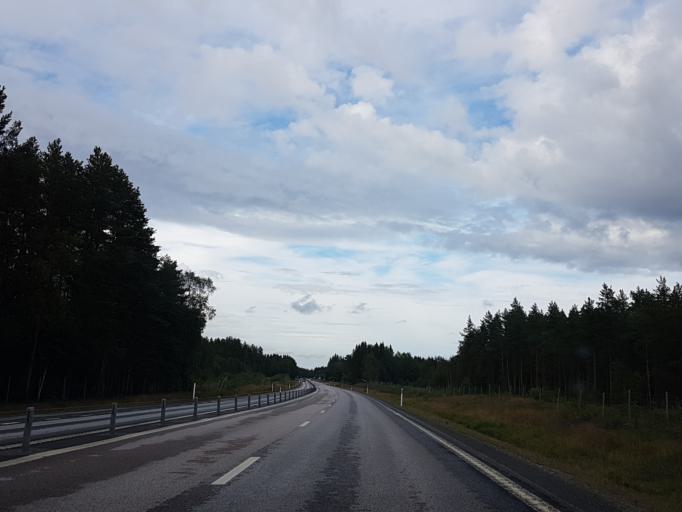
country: SE
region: Vaesterbotten
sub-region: Umea Kommun
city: Saevar
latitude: 63.9055
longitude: 20.5812
